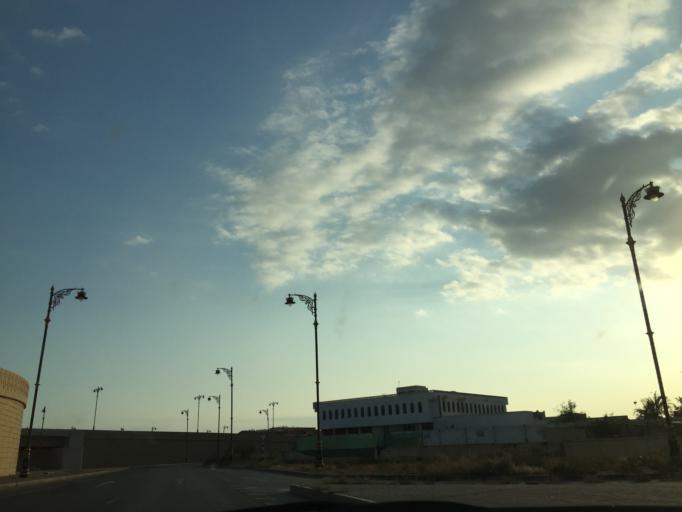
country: OM
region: Zufar
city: Salalah
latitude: 17.0179
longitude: 54.0564
